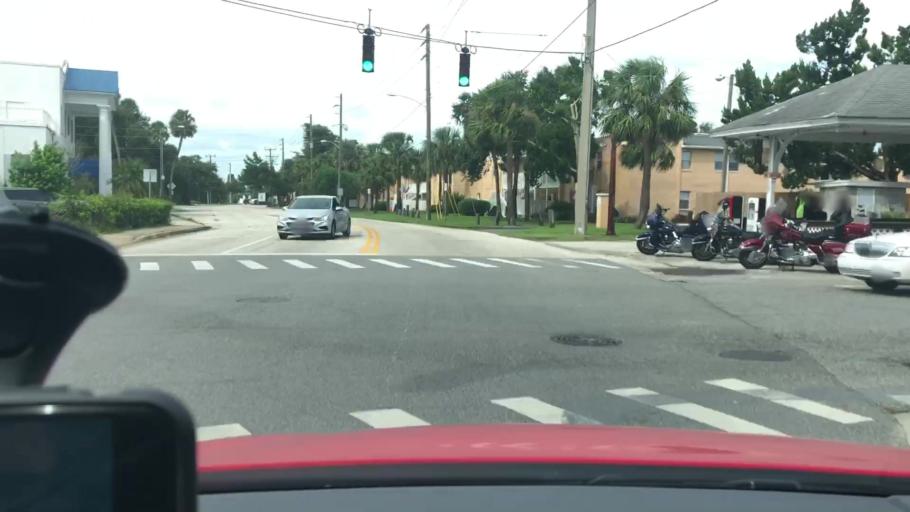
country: US
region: Florida
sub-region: Volusia County
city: Daytona Beach
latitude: 29.1983
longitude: -81.0133
